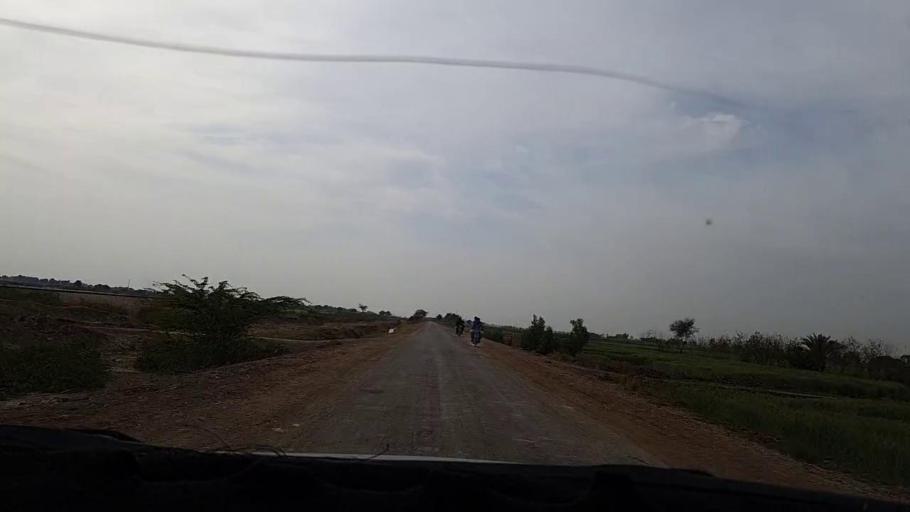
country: PK
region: Sindh
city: Pithoro
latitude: 25.5168
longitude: 69.2650
